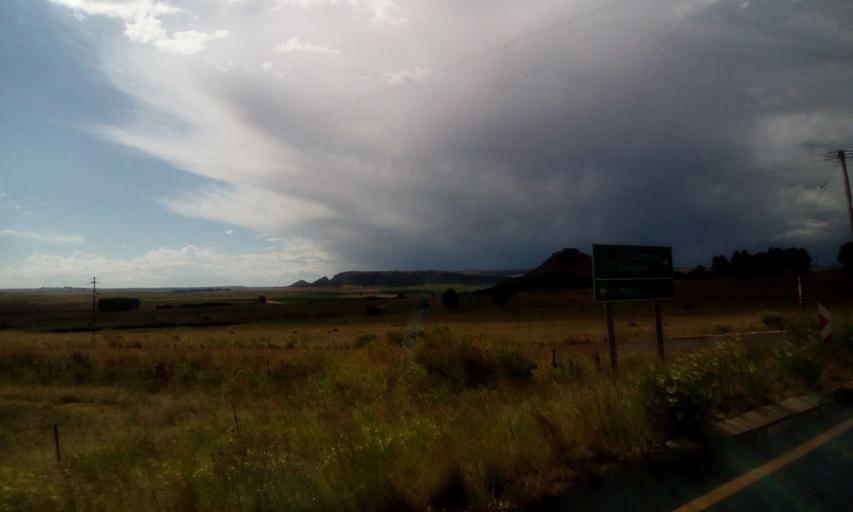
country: LS
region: Maseru
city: Maseru
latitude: -29.2670
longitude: 27.4342
